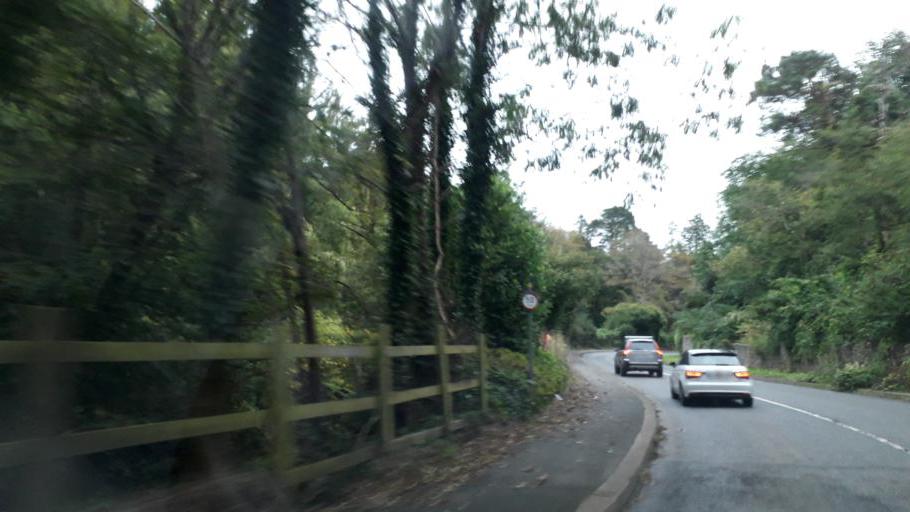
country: IE
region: Leinster
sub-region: Wicklow
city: Enniskerry
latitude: 53.1906
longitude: -6.1565
